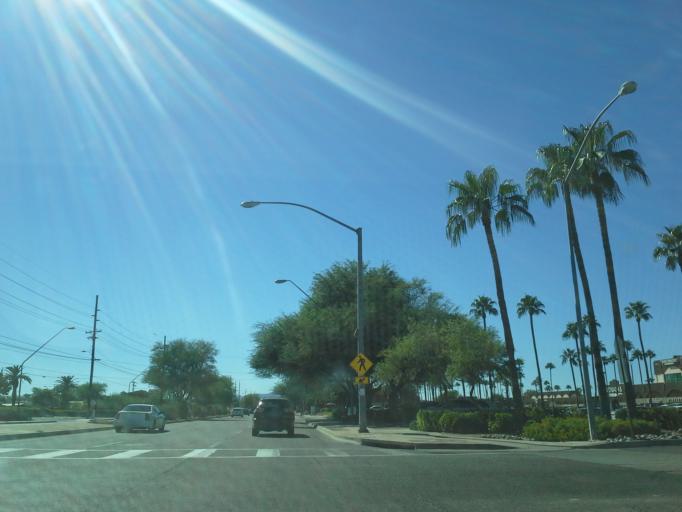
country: US
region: Arizona
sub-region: Pima County
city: Tucson
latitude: 32.2508
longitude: -110.8883
